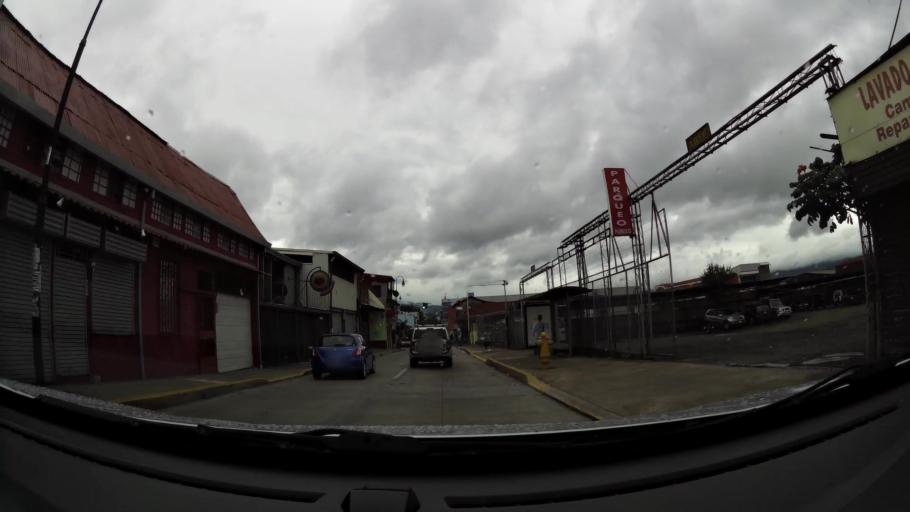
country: CR
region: San Jose
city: San Jose
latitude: 9.9297
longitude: -84.0777
